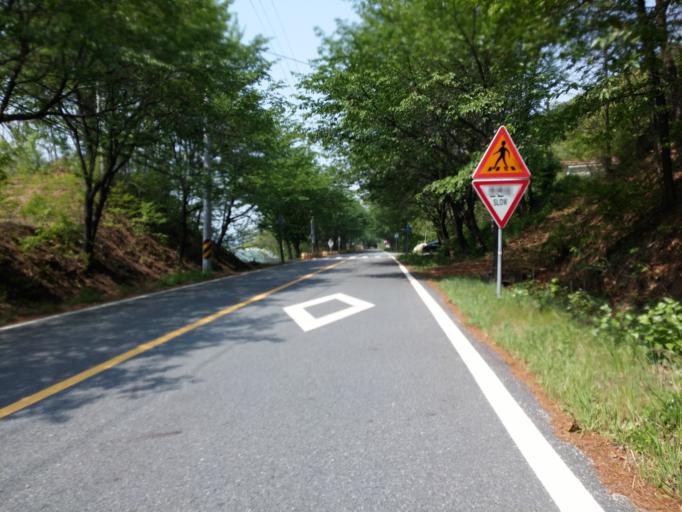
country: KR
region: Daejeon
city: Sintansin
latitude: 36.4159
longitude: 127.5363
